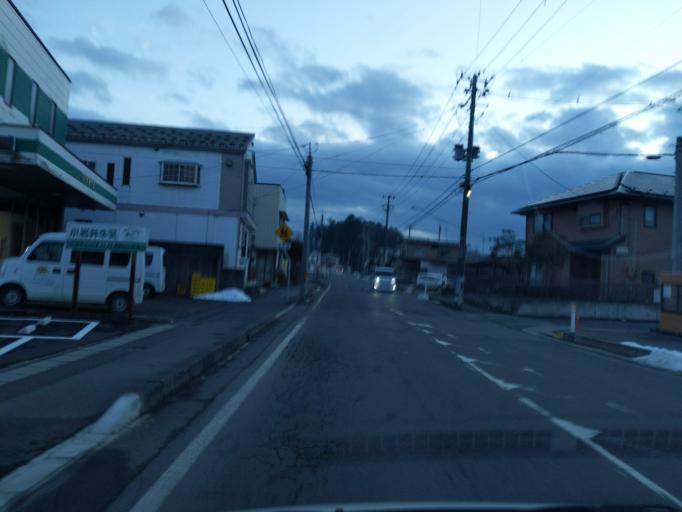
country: JP
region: Iwate
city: Mizusawa
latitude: 39.1272
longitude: 141.1411
